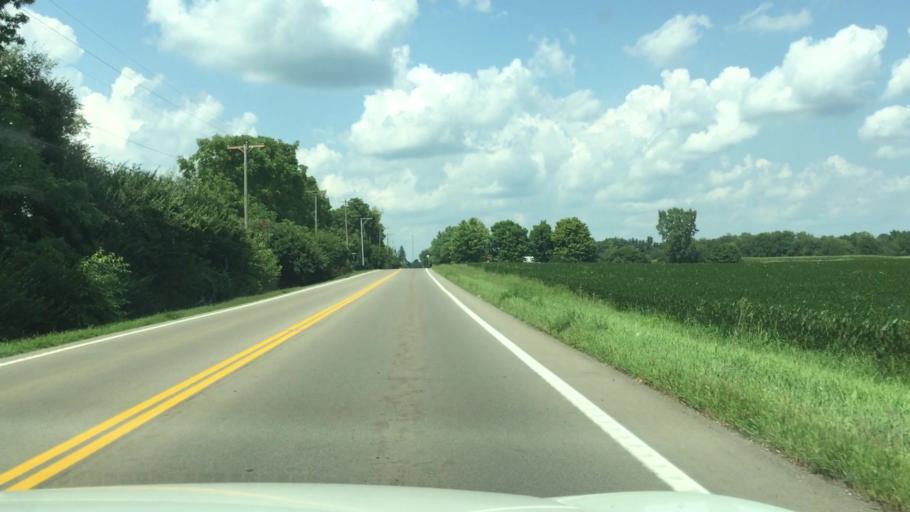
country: US
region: Ohio
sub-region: Clark County
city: Northridge
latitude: 39.9592
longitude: -83.7614
